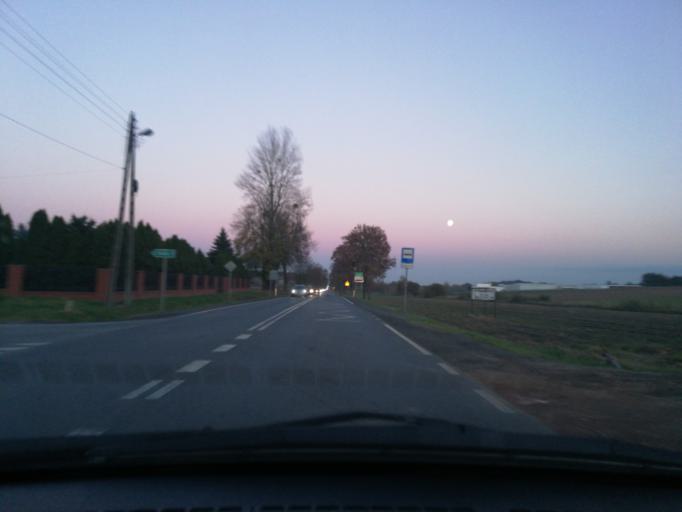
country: PL
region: Lodz Voivodeship
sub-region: Powiat brzezinski
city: Brzeziny
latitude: 51.8058
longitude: 19.6773
